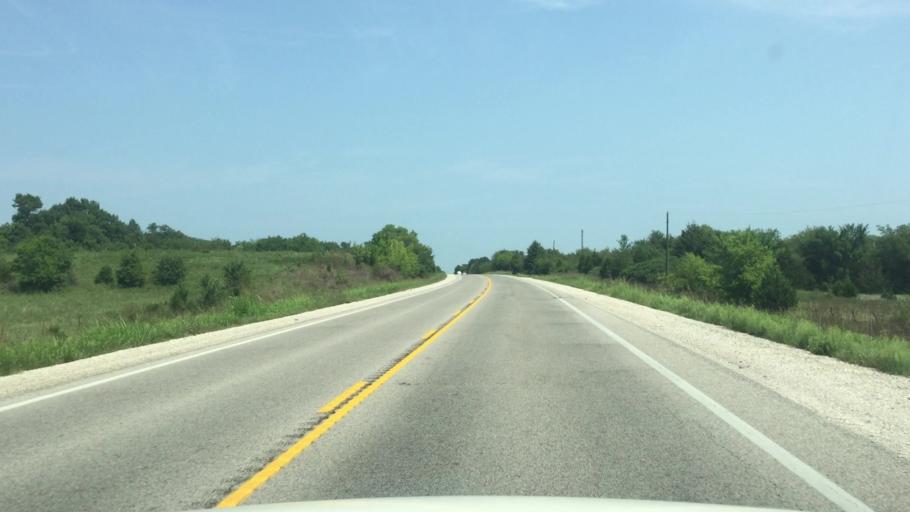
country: US
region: Kansas
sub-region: Montgomery County
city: Coffeyville
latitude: 37.1385
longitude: -95.5768
